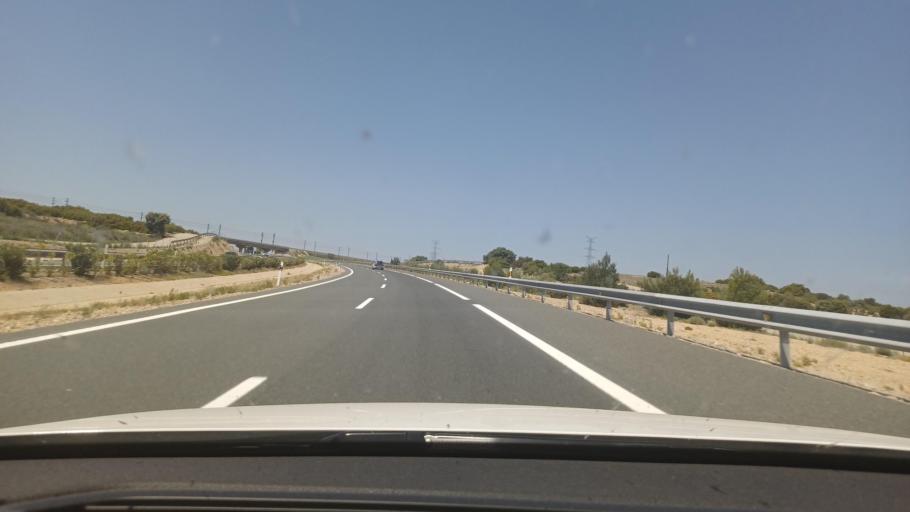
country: ES
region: Castille-La Mancha
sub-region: Provincia de Albacete
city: Alpera
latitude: 38.8809
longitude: -1.2499
